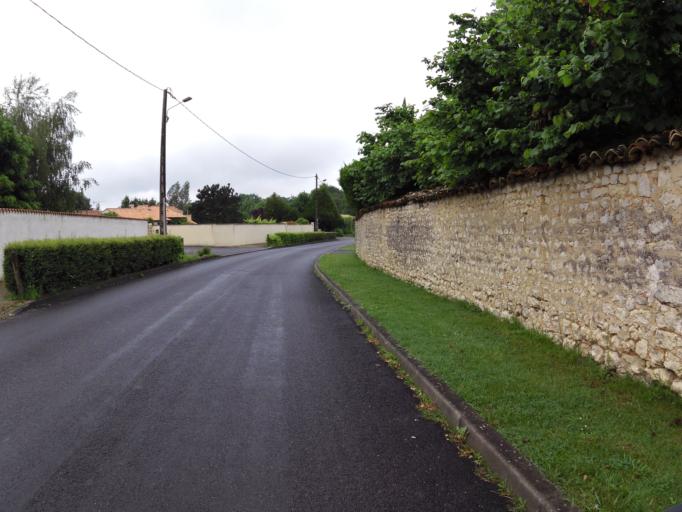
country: FR
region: Poitou-Charentes
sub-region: Departement de la Charente
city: Balzac
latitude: 45.7112
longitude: 0.1366
